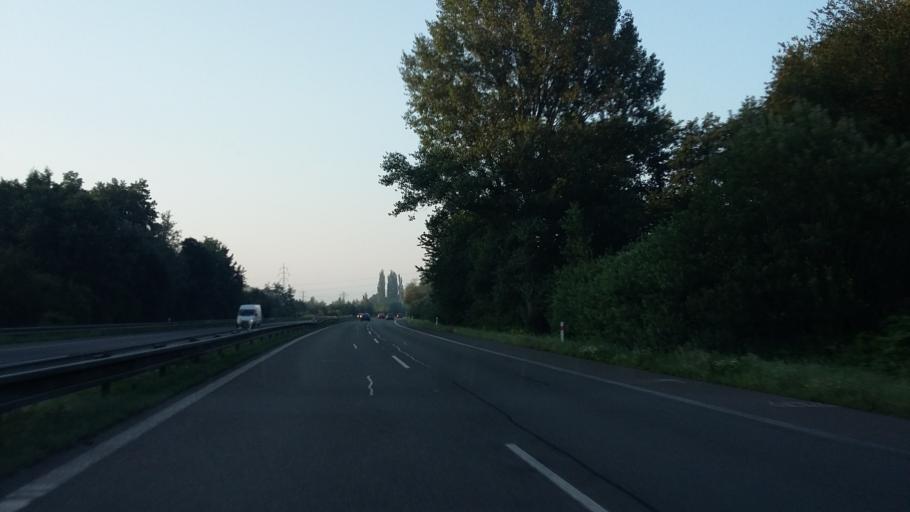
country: CZ
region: Central Bohemia
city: Kosmonosy
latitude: 50.4472
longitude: 14.9395
